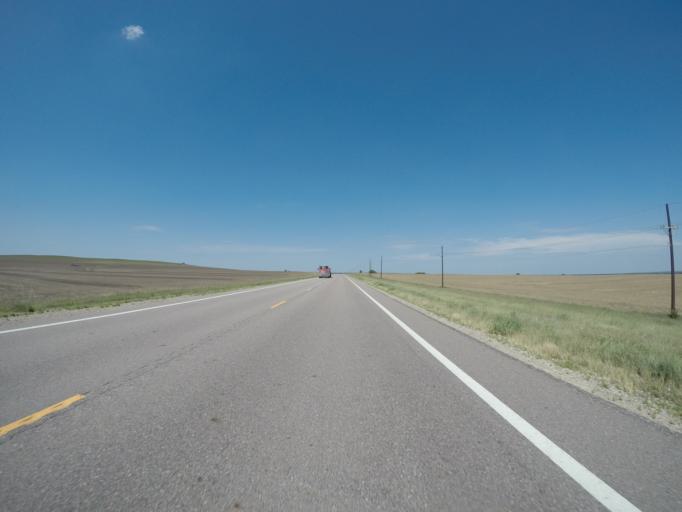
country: US
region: Kansas
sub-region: Osborne County
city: Osborne
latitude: 39.5101
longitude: -98.6758
